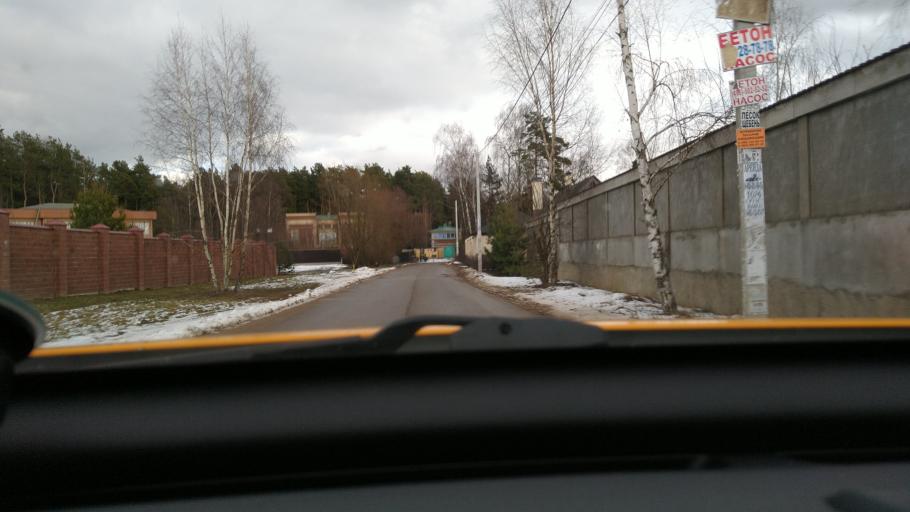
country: RU
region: Moskovskaya
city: Petrovo-Dal'neye
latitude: 55.7687
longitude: 37.2064
